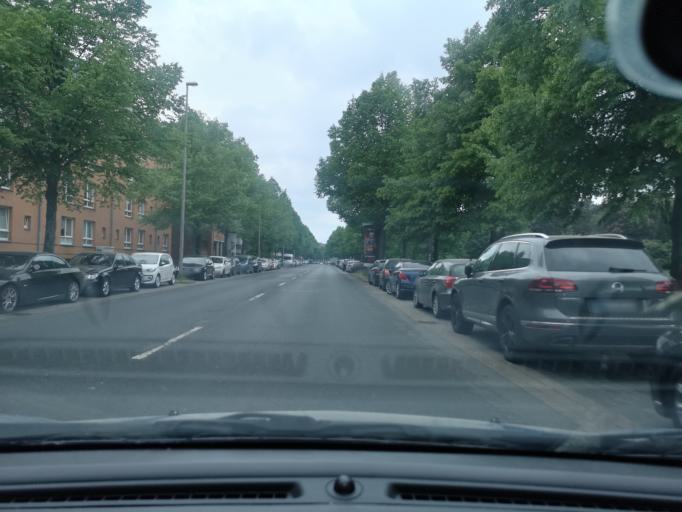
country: DE
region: Lower Saxony
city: Auf der Horst
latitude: 52.4019
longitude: 9.6659
